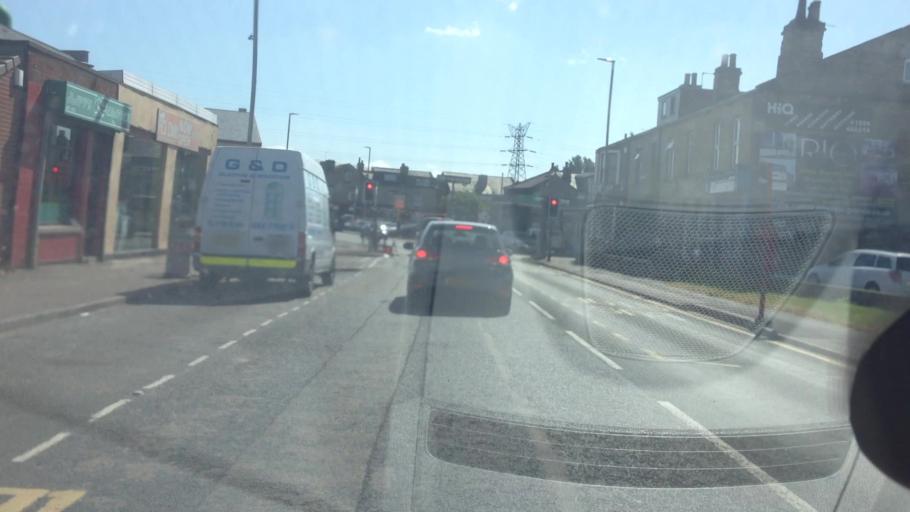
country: GB
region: England
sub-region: Kirklees
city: Dewsbury
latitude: 53.6799
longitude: -1.6578
